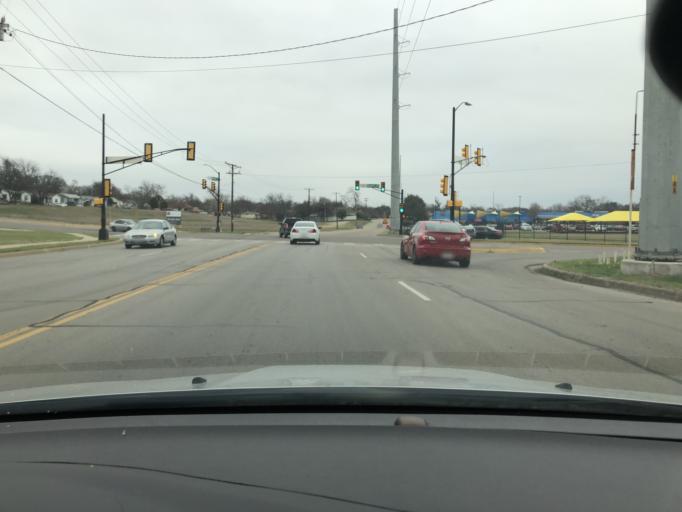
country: US
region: Texas
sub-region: Tarrant County
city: Fort Worth
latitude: 32.7270
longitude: -97.2907
